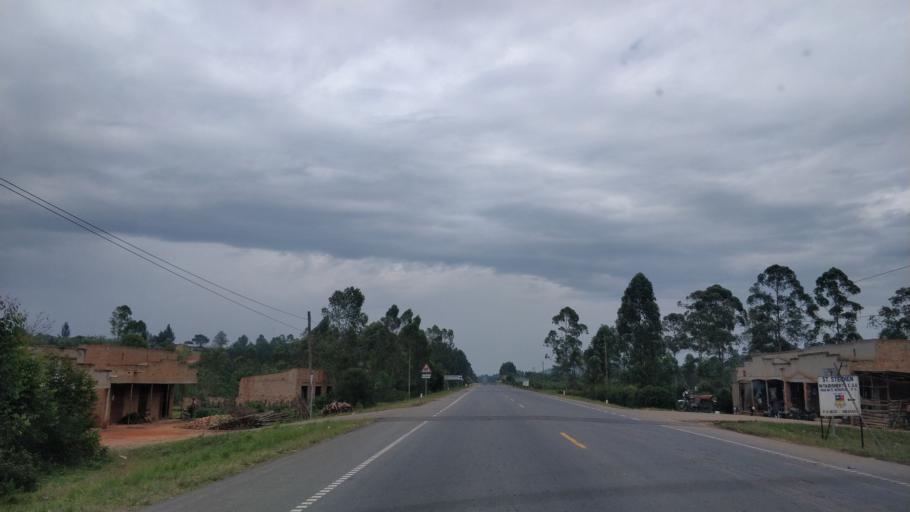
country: UG
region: Western Region
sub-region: Sheema District
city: Kibingo
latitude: -0.6721
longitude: 30.4304
